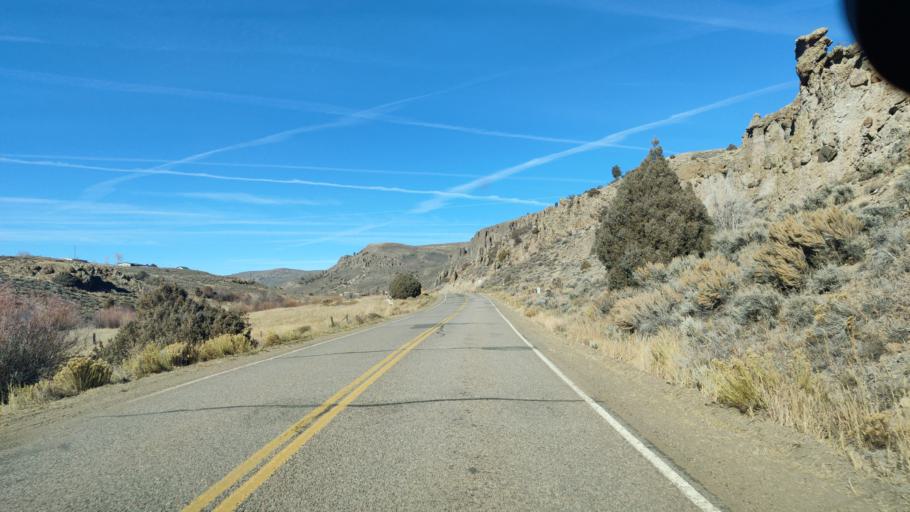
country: US
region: Colorado
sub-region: Gunnison County
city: Gunnison
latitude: 38.5728
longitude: -106.9611
